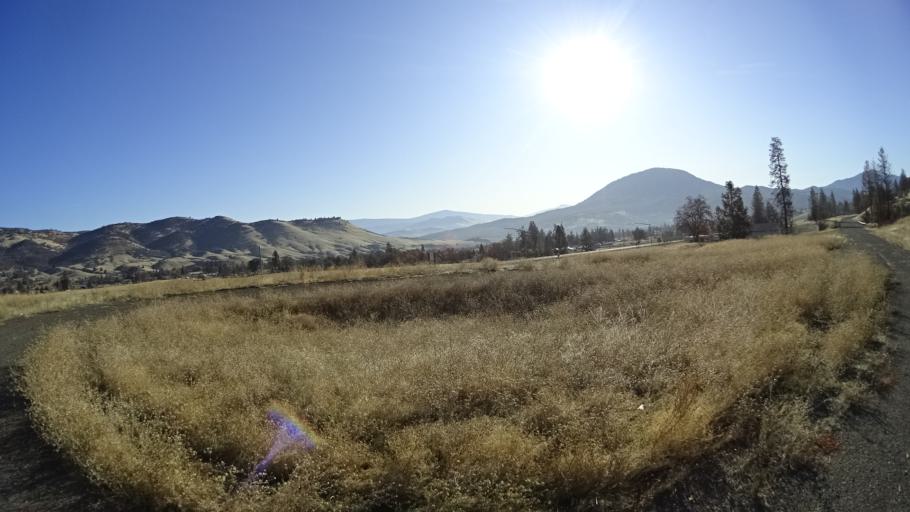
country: US
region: California
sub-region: Siskiyou County
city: Yreka
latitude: 41.9096
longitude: -122.5704
